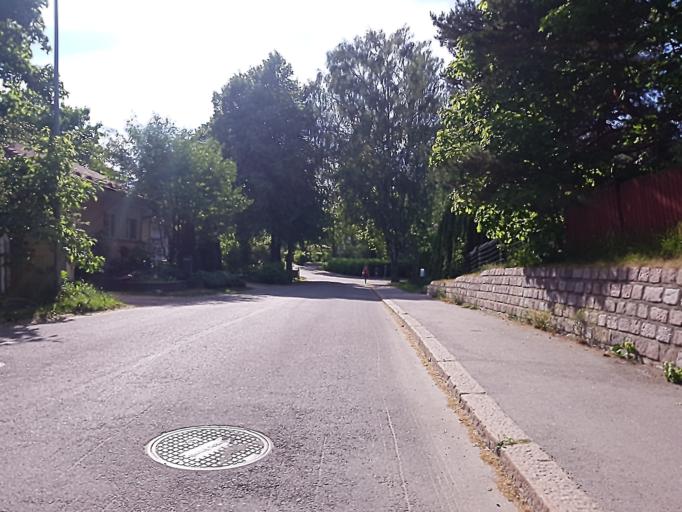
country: FI
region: Uusimaa
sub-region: Helsinki
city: Helsinki
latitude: 60.2438
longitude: 24.9547
